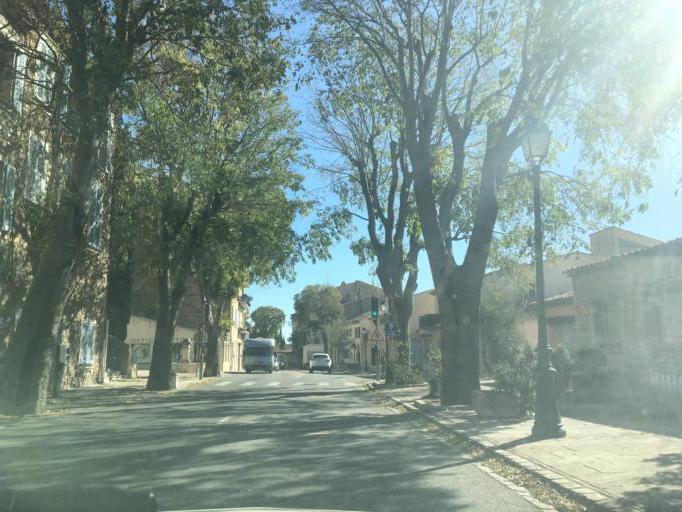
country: FR
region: Provence-Alpes-Cote d'Azur
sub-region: Departement du Var
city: Grimaud
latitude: 43.2730
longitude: 6.5209
